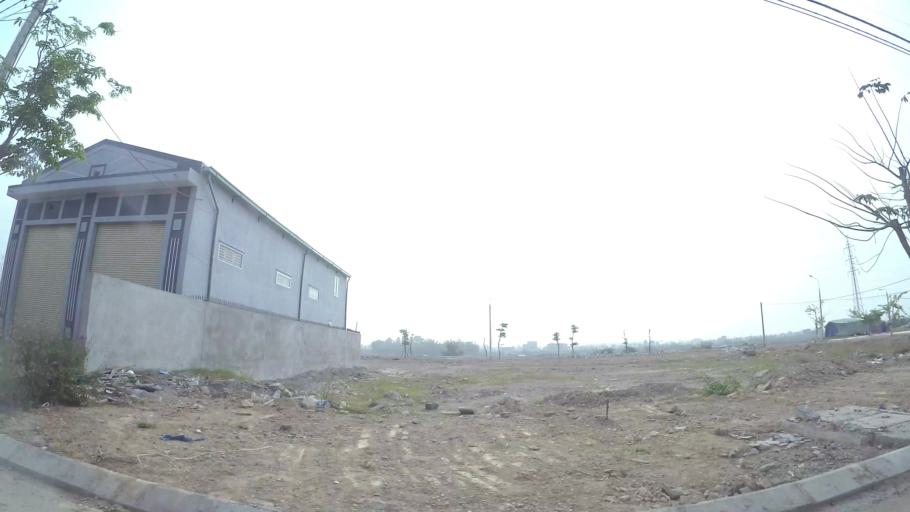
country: VN
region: Da Nang
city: Ngu Hanh Son
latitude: 16.0133
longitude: 108.2311
